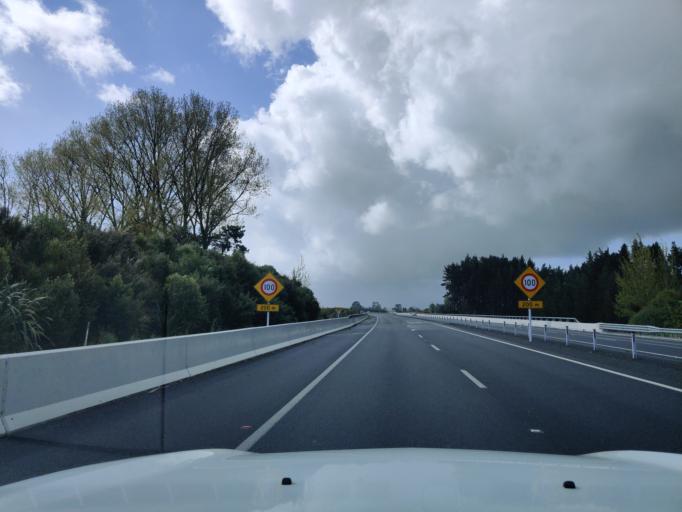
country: NZ
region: Waikato
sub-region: Waipa District
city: Cambridge
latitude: -37.8872
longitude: 175.4950
